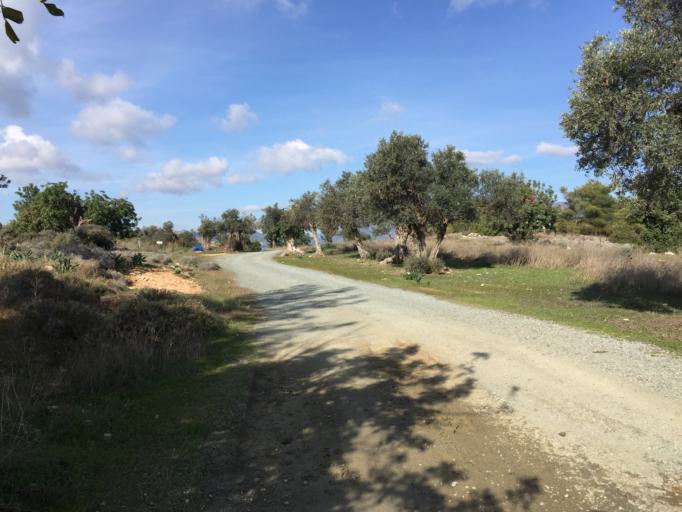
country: CY
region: Larnaka
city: Agios Tychon
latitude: 34.7472
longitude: 33.1265
